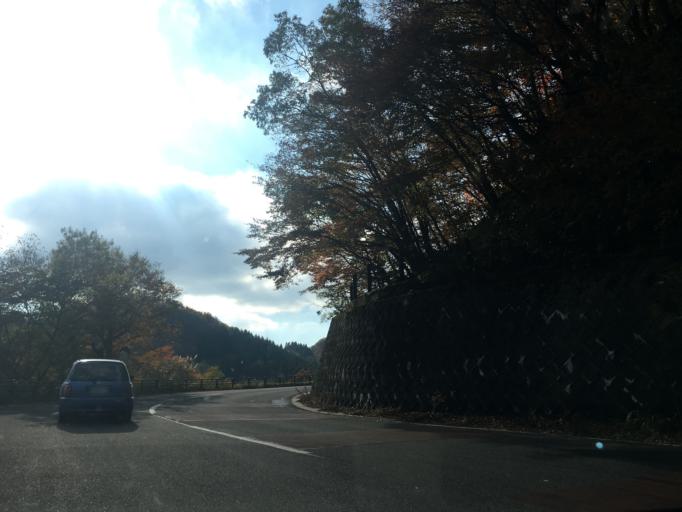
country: JP
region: Fukushima
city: Sukagawa
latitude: 37.2666
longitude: 140.1183
